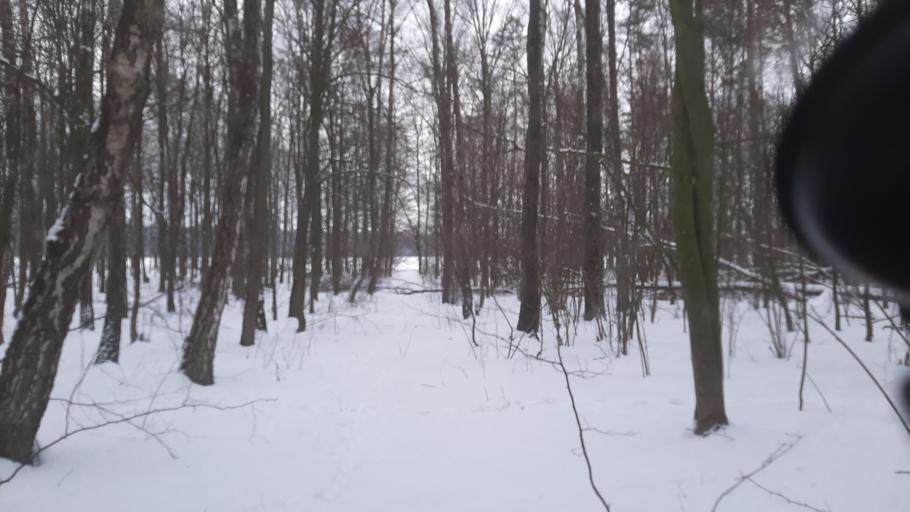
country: PL
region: Lublin Voivodeship
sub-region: Powiat lubelski
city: Garbow
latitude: 51.3733
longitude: 22.3918
